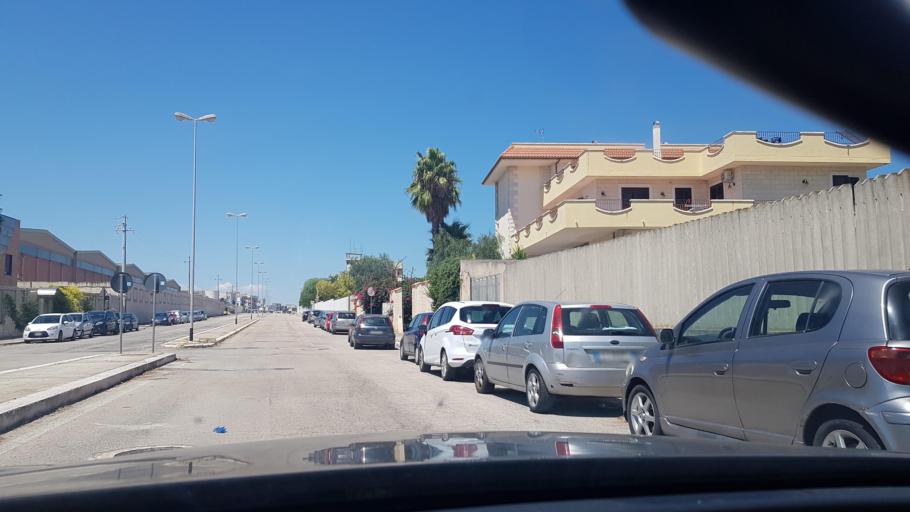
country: IT
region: Apulia
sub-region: Provincia di Barletta - Andria - Trani
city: Barletta
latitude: 41.3037
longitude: 16.3298
